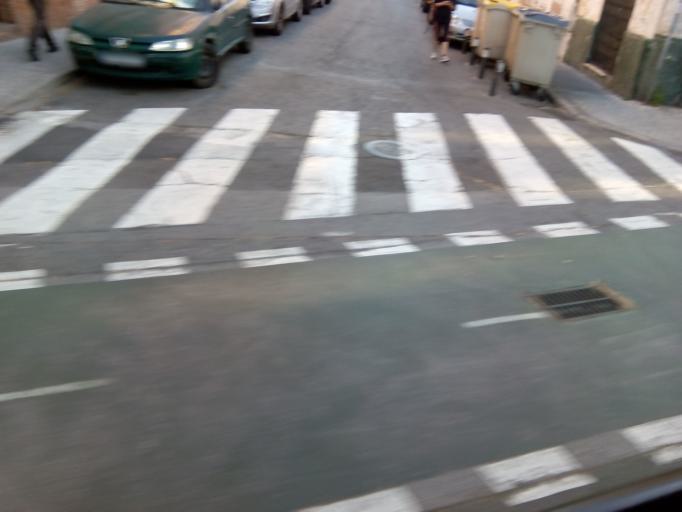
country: ES
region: Andalusia
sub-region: Provincia de Sevilla
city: Sevilla
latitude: 37.4037
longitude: -5.9946
